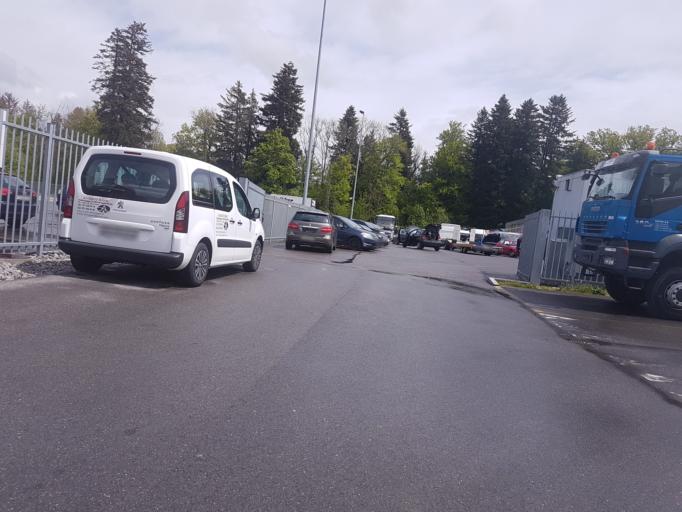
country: CH
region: Vaud
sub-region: Ouest Lausannois District
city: Bussigny
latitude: 46.5633
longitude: 6.5251
